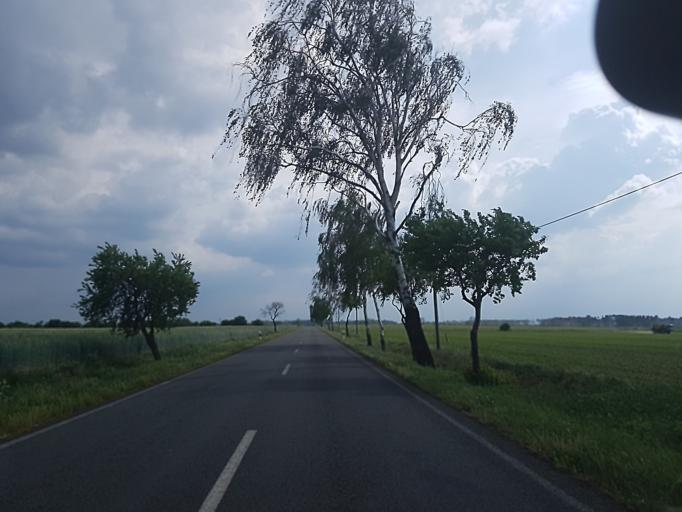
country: DE
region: Saxony-Anhalt
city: Rodleben
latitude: 52.0024
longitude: 12.2331
